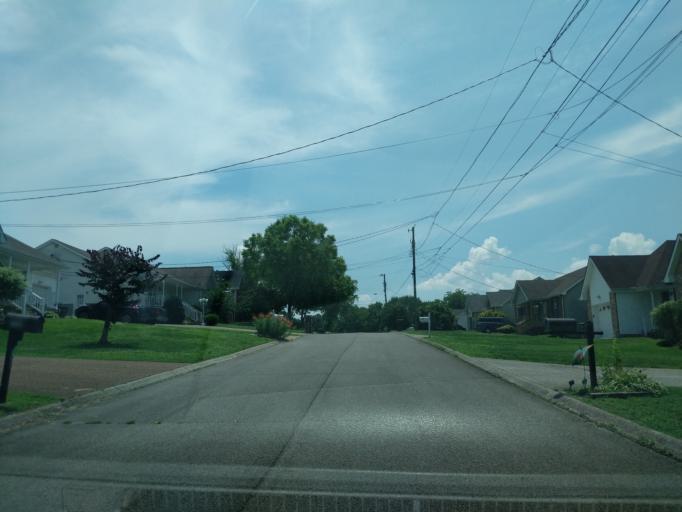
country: US
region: Tennessee
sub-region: Davidson County
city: Lakewood
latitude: 36.2410
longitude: -86.6354
